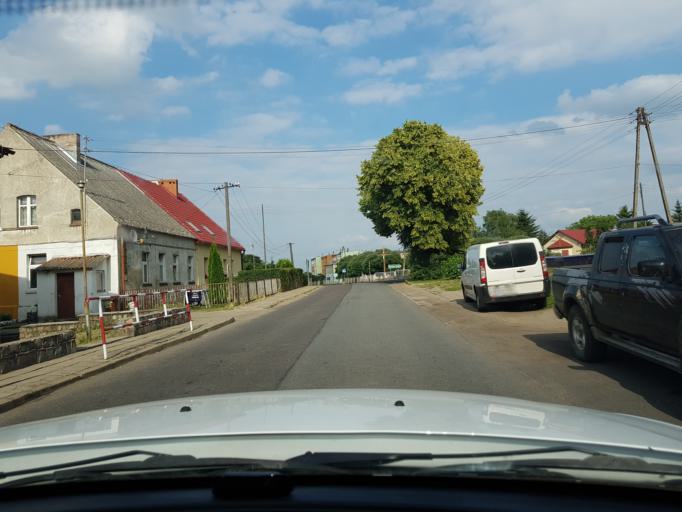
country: PL
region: West Pomeranian Voivodeship
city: Trzcinsko Zdroj
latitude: 53.0185
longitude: 14.5600
